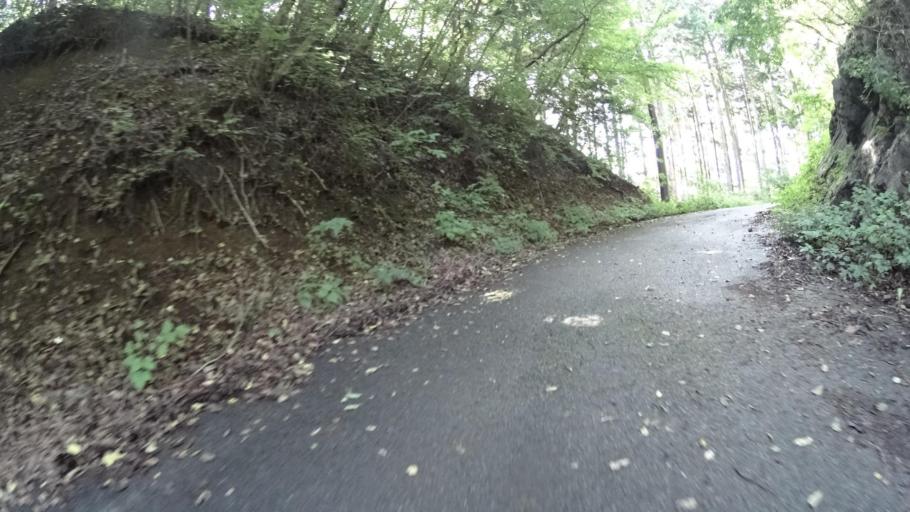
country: JP
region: Yamanashi
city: Uenohara
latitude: 35.7435
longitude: 139.0622
